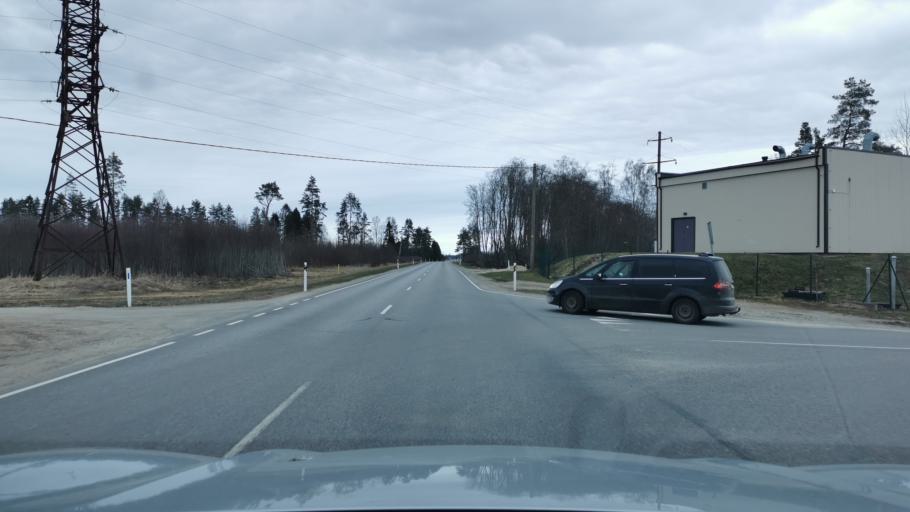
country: EE
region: Ida-Virumaa
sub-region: Puessi linn
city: Pussi
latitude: 59.3615
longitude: 27.0258
